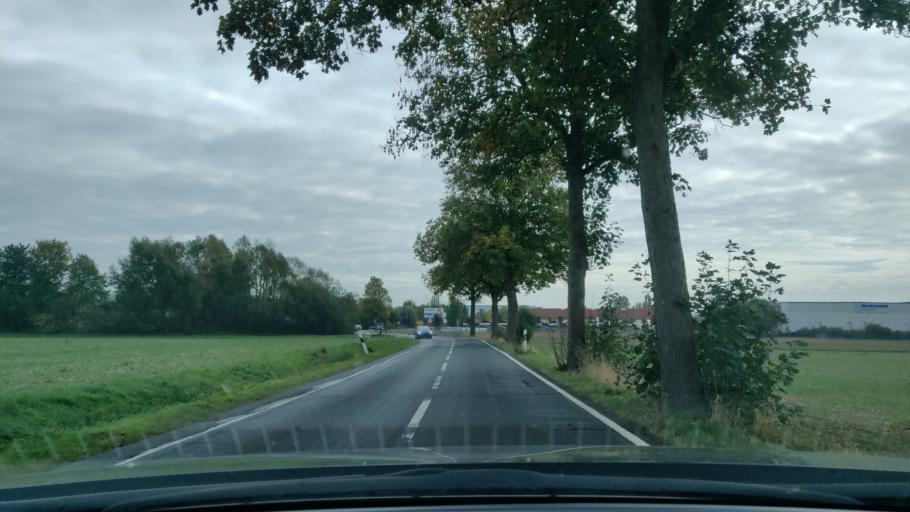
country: DE
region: Hesse
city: Schwalmstadt
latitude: 50.9239
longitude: 9.2233
